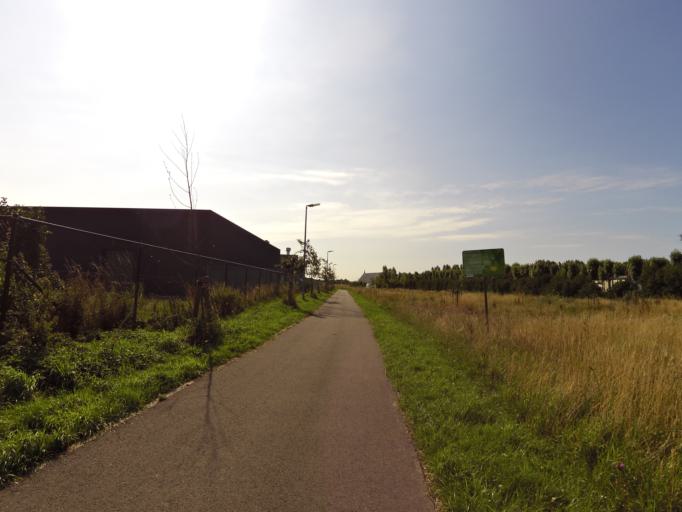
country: BE
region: Flanders
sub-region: Provincie West-Vlaanderen
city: Jabbeke
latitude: 51.1821
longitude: 3.1072
